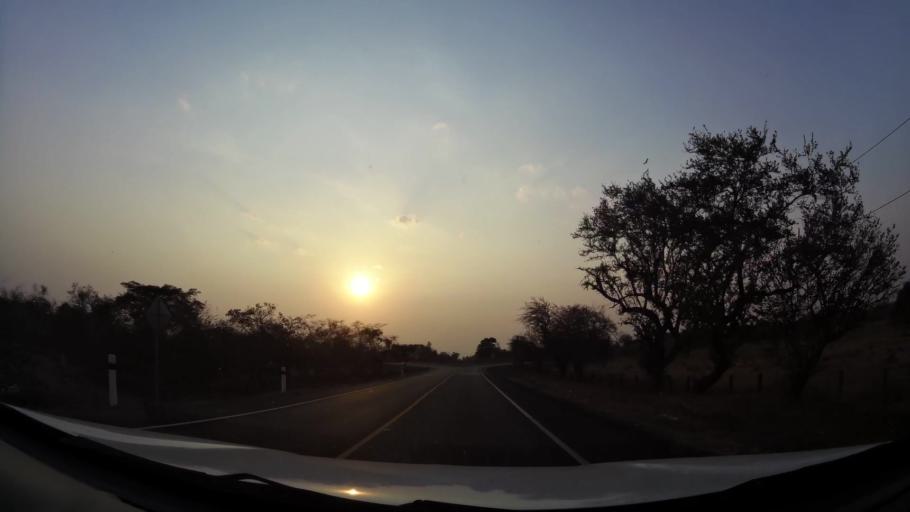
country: NI
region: Leon
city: La Paz Centro
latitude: 12.3351
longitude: -86.6543
